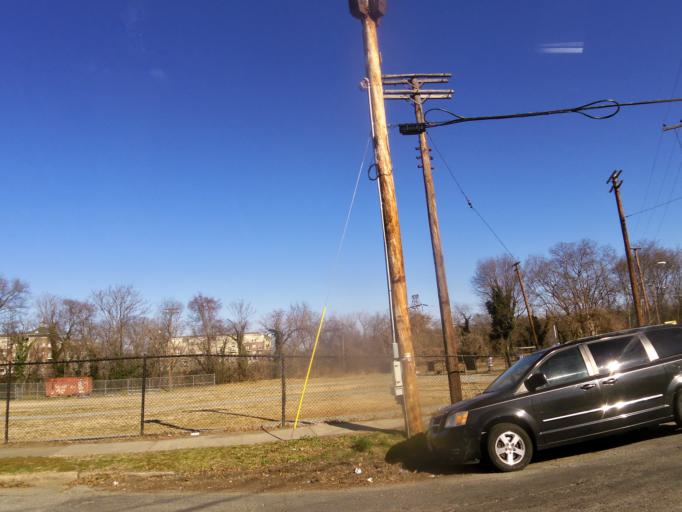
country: US
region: Virginia
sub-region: City of Richmond
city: Richmond
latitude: 37.5539
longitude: -77.4382
